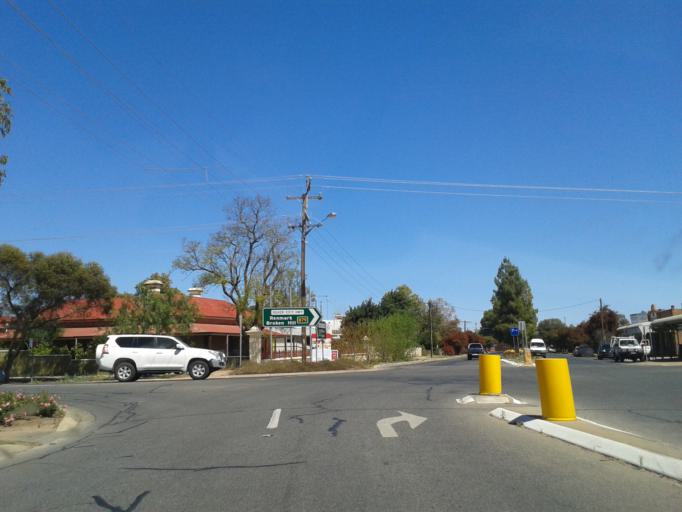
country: AU
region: New South Wales
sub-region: Wentworth
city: Dareton
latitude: -34.1071
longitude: 141.9181
